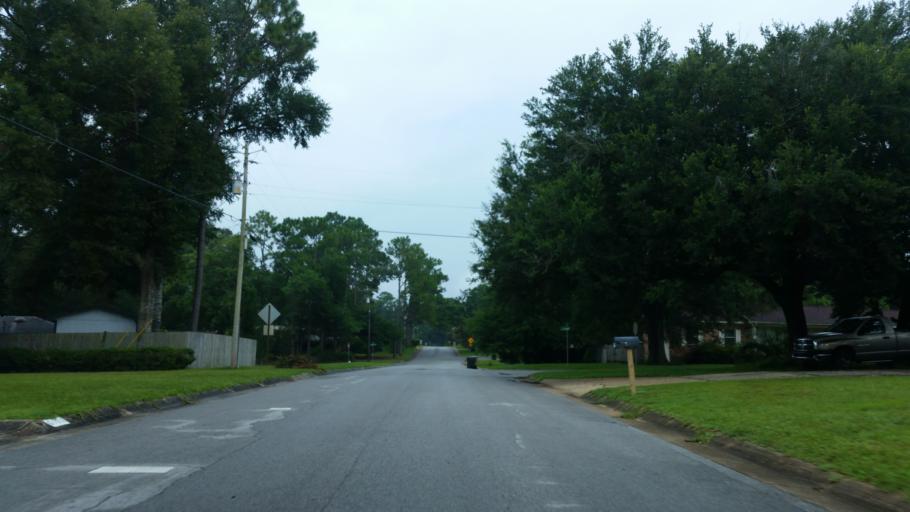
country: US
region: Florida
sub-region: Escambia County
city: Brent
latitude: 30.4916
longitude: -87.2394
